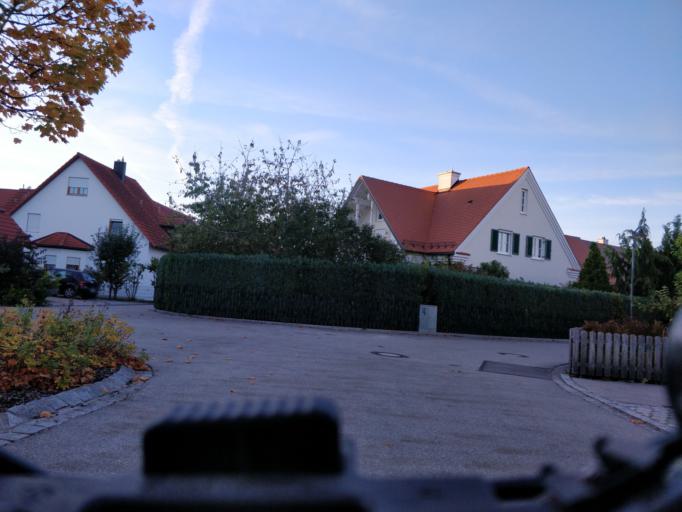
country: DE
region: Bavaria
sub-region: Swabia
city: Mering
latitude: 48.2774
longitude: 10.9743
